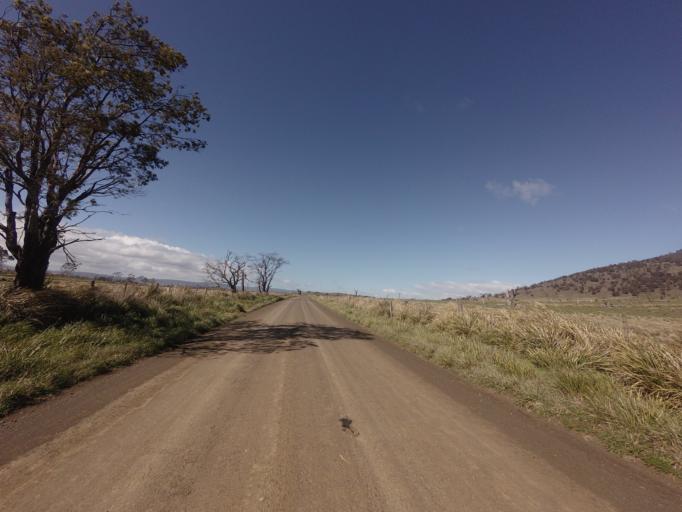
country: AU
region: Tasmania
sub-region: Northern Midlands
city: Evandale
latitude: -41.9228
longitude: 147.4039
